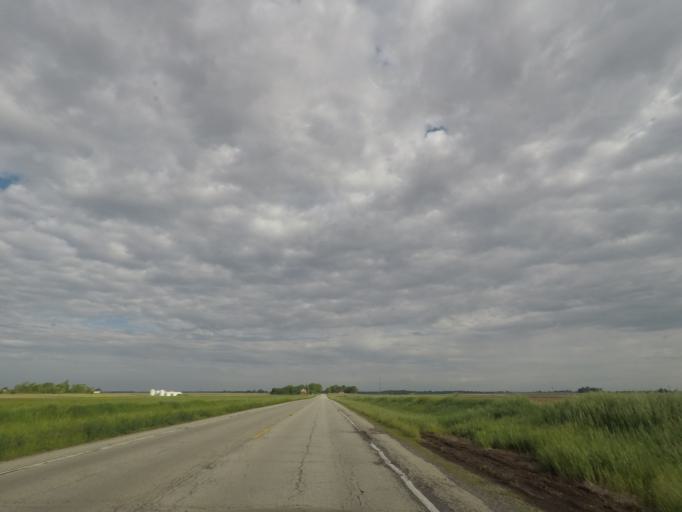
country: US
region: Illinois
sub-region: Logan County
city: Lincoln
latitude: 40.0891
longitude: -89.3083
